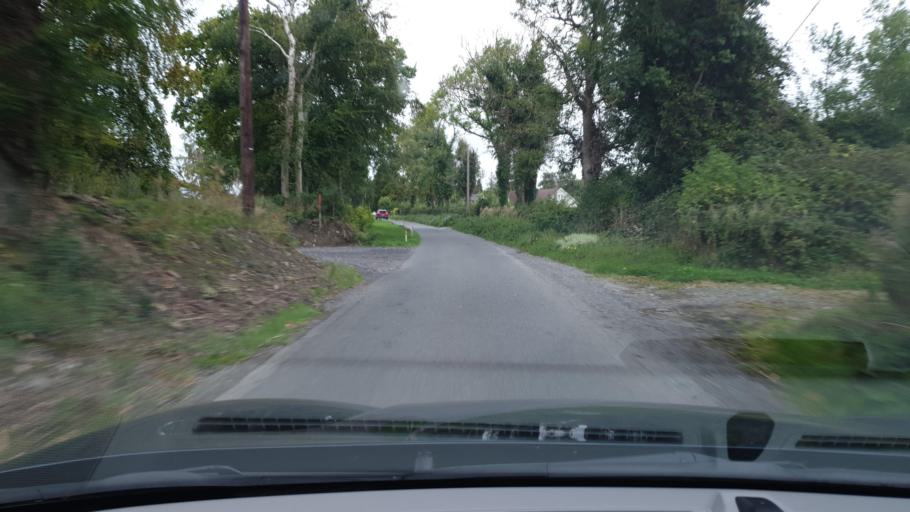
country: IE
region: Leinster
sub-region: An Mhi
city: Ratoath
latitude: 53.5255
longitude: -6.4996
